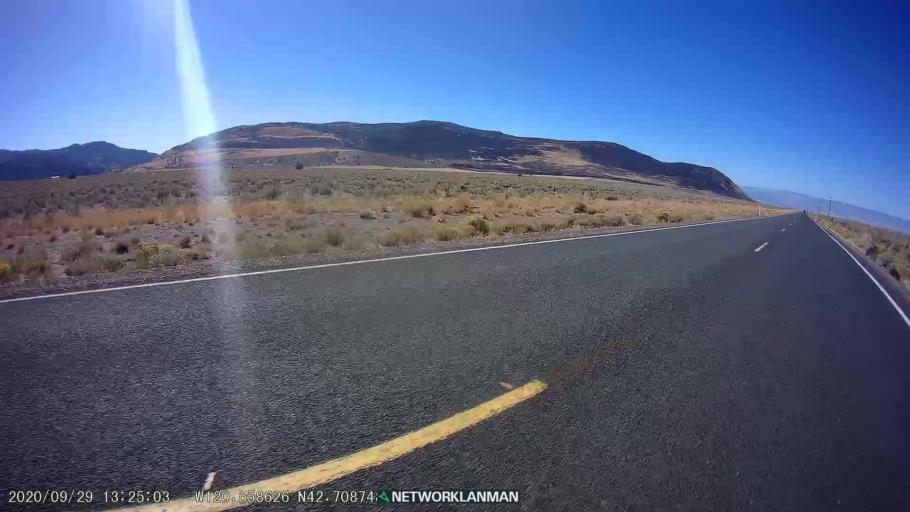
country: US
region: Oregon
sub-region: Lake County
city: Lakeview
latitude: 42.7086
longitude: -120.5570
